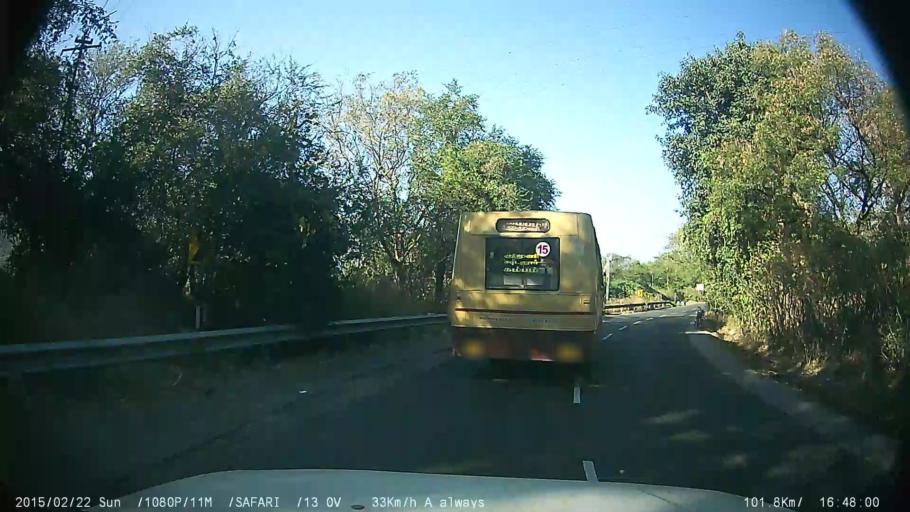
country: IN
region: Tamil Nadu
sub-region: Theni
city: Gudalur
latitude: 9.6254
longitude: 77.1949
